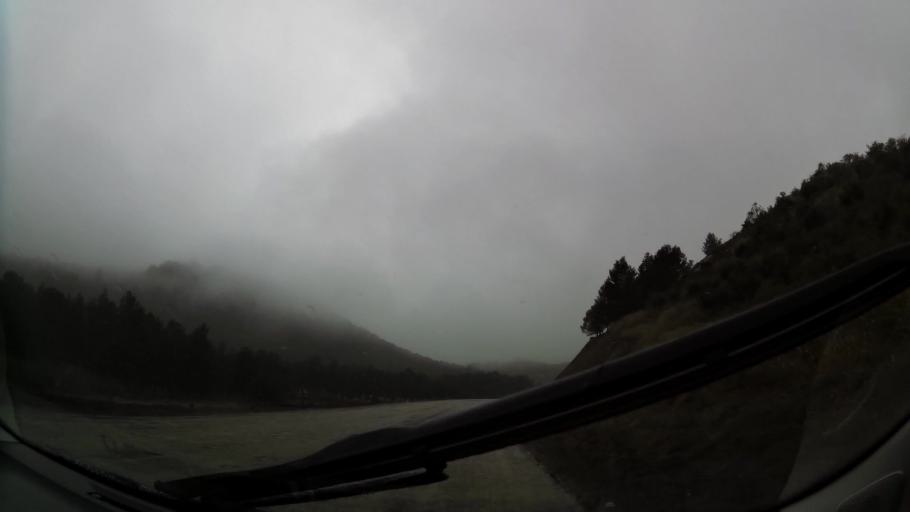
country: MA
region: Taza-Al Hoceima-Taounate
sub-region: Taza
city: Aknoul
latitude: 34.7573
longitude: -3.8030
